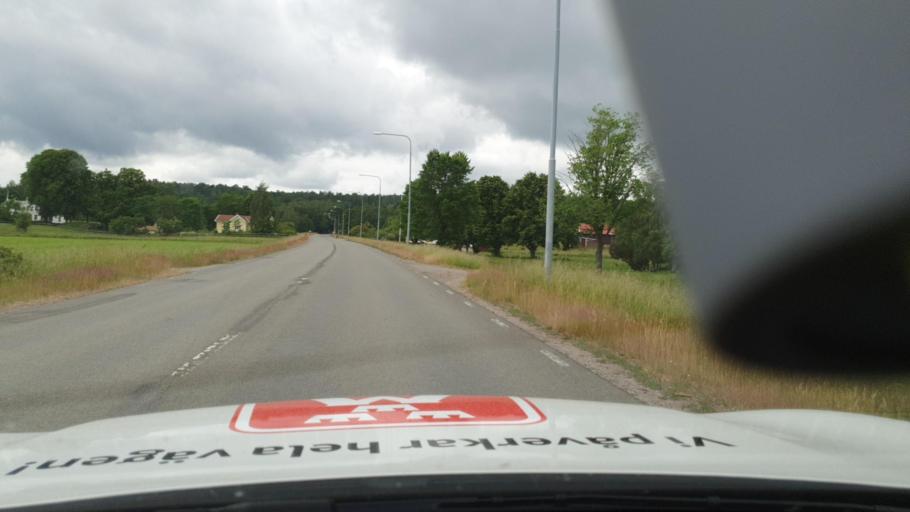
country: SE
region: Vaestra Goetaland
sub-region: Hjo Kommun
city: Hjo
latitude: 58.2904
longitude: 14.2694
